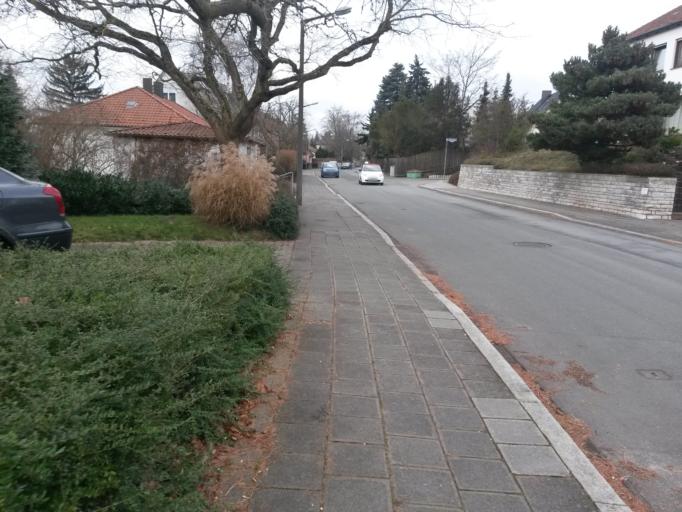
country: DE
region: Bavaria
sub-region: Regierungsbezirk Mittelfranken
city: Furth
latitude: 49.4731
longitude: 11.0098
